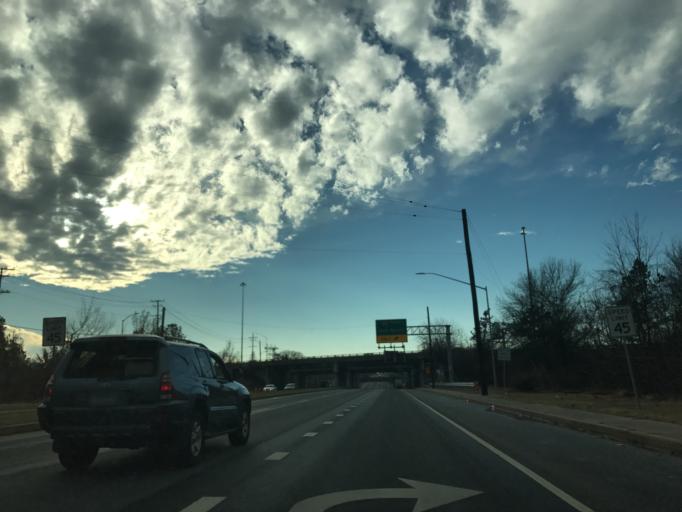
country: US
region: Maryland
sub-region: Baltimore County
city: Rosedale
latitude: 39.2980
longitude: -76.5010
